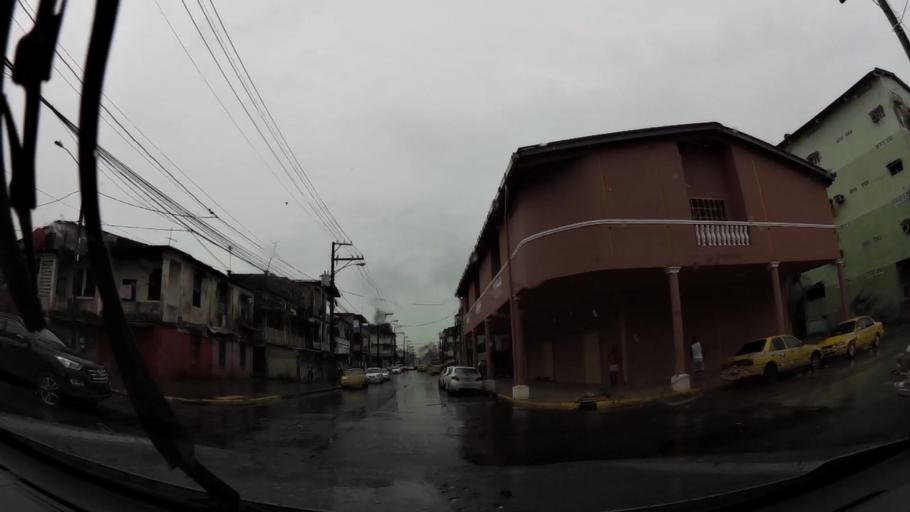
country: PA
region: Colon
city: Colon
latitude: 9.3593
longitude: -79.9000
